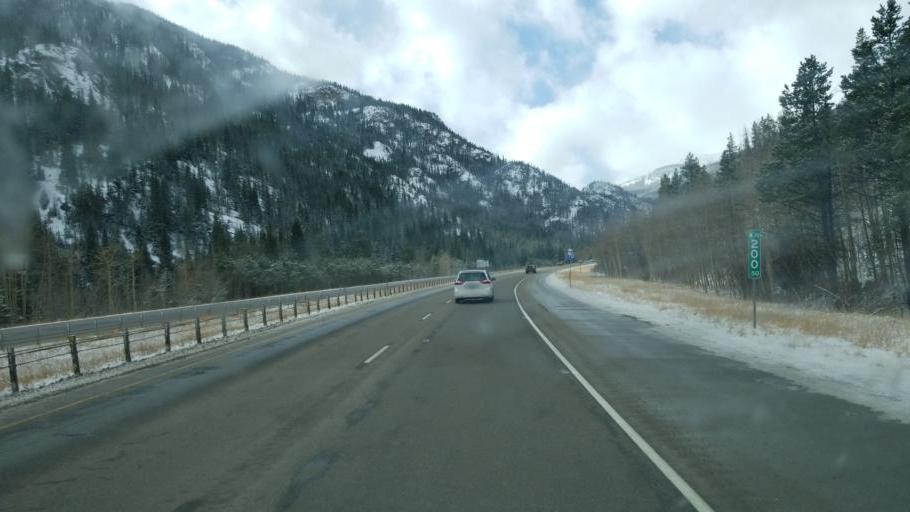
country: US
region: Colorado
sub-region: Summit County
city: Frisco
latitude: 39.5713
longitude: -106.1151
